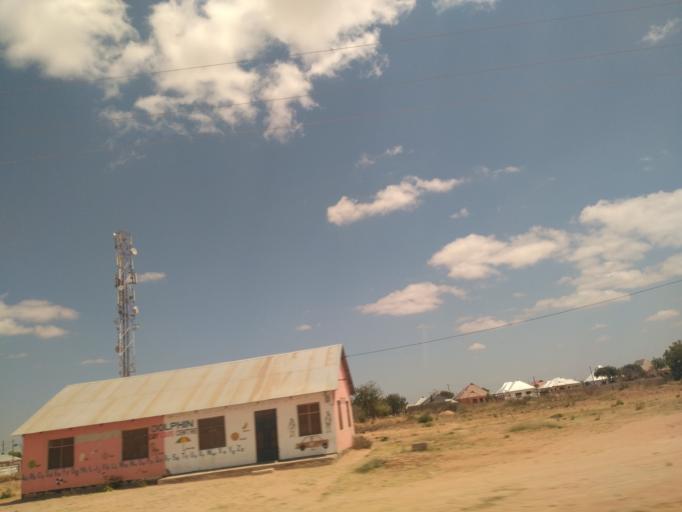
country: TZ
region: Dodoma
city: Kisasa
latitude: -6.1656
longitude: 35.7912
